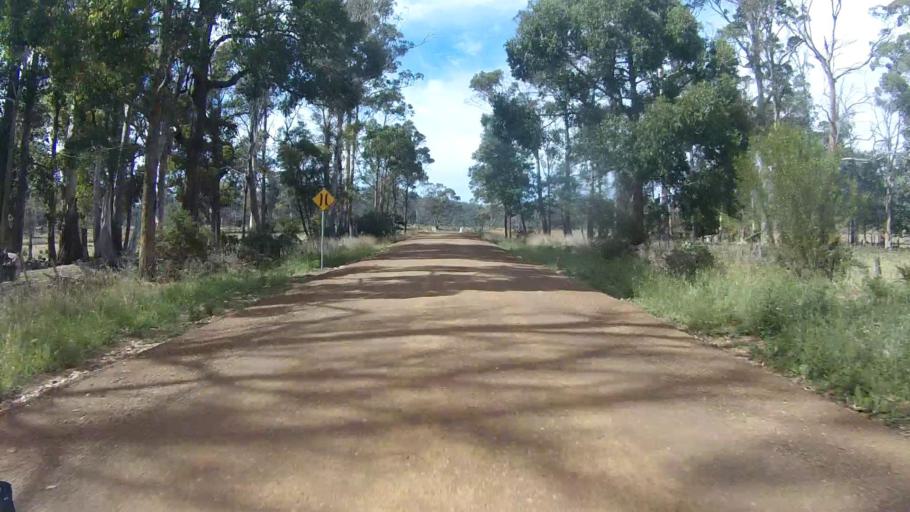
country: AU
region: Tasmania
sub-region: Sorell
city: Sorell
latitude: -42.6417
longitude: 147.9005
